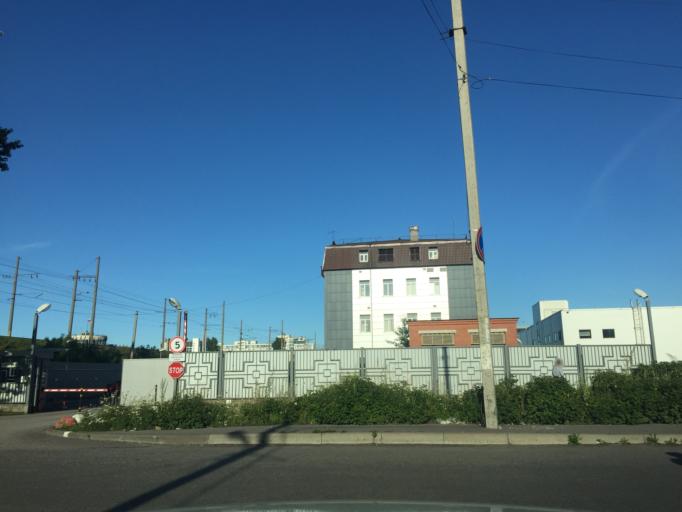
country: RU
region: St.-Petersburg
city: Admiralteisky
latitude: 59.8824
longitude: 30.3122
